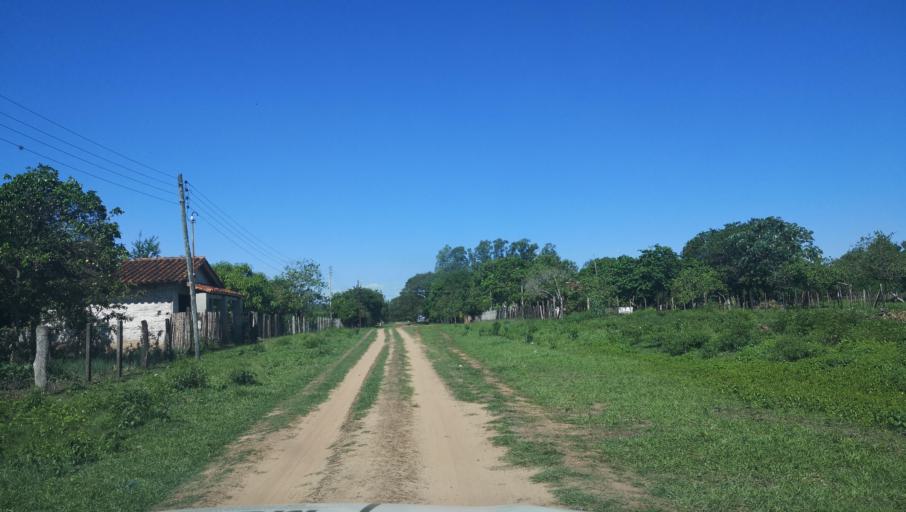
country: PY
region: Caaguazu
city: Carayao
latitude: -25.1931
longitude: -56.4038
